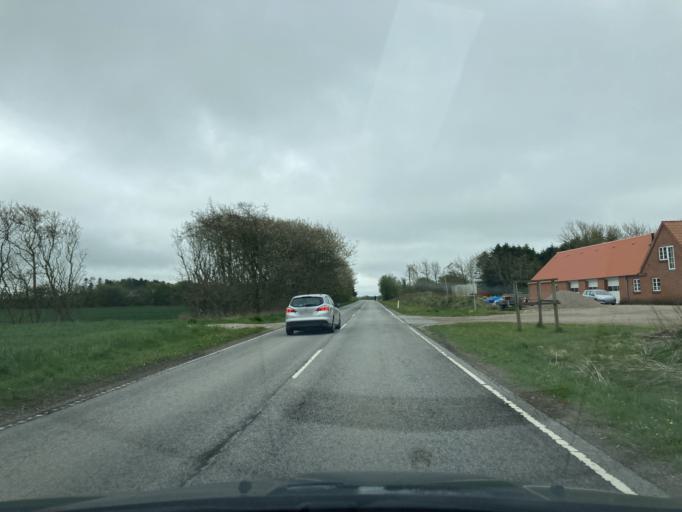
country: DK
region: North Denmark
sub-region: Thisted Kommune
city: Hurup
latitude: 56.8476
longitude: 8.3658
